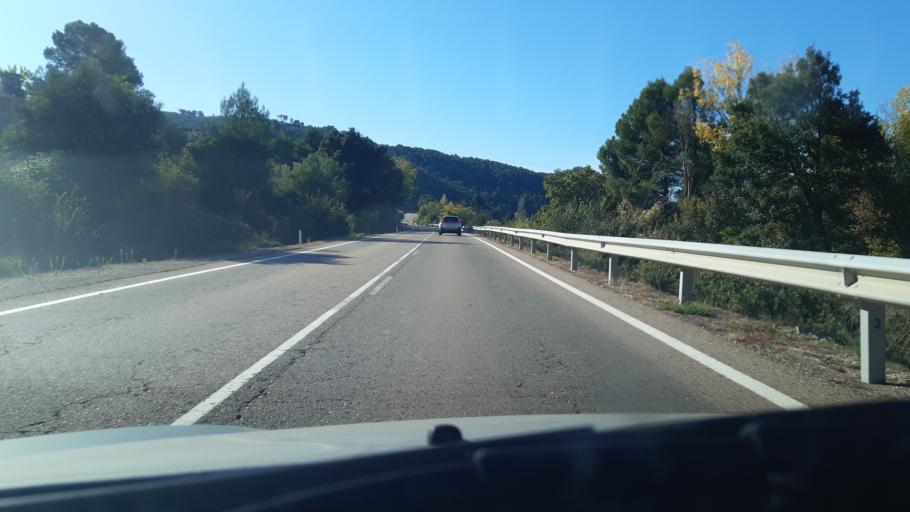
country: ES
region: Aragon
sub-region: Provincia de Teruel
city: Valderrobres
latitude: 40.8828
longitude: 0.1280
